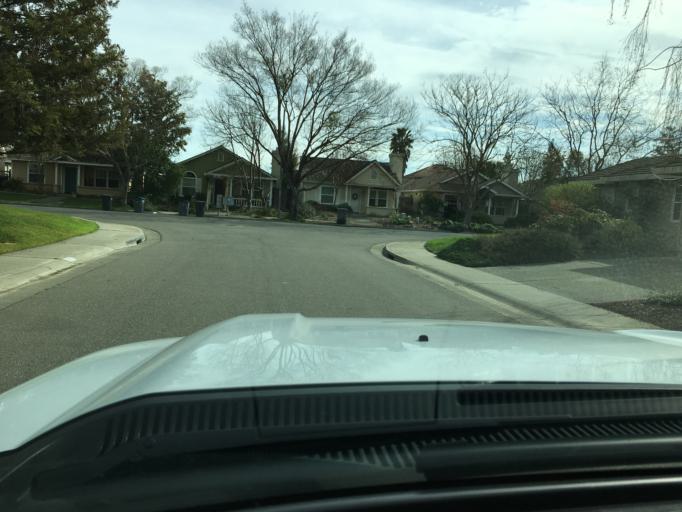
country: US
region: California
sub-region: Yolo County
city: Davis
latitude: 38.5559
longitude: -121.7767
